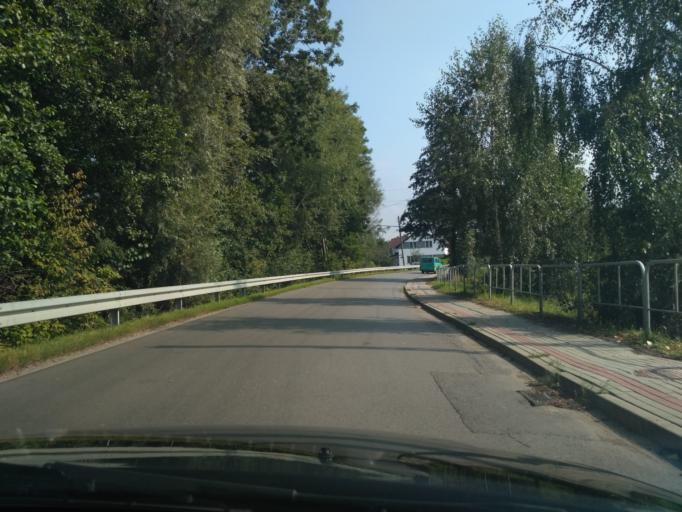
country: PL
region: Subcarpathian Voivodeship
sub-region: Powiat rzeszowski
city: Niechobrz
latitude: 50.0026
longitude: 21.8916
